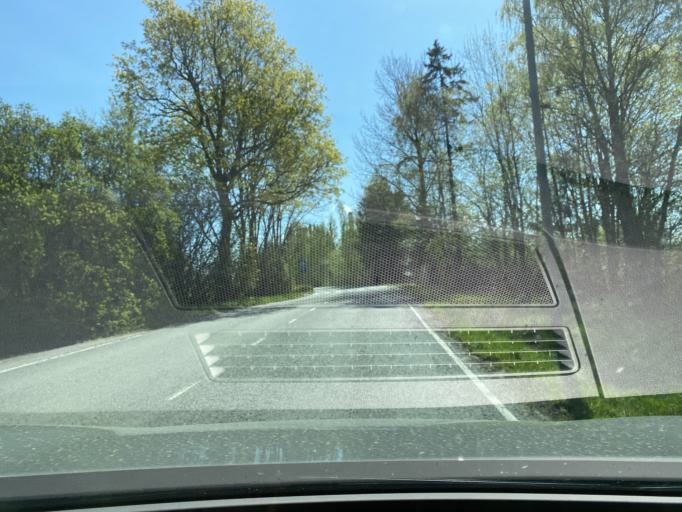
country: FI
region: Pirkanmaa
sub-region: Lounais-Pirkanmaa
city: Vammala
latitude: 61.3506
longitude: 22.8775
